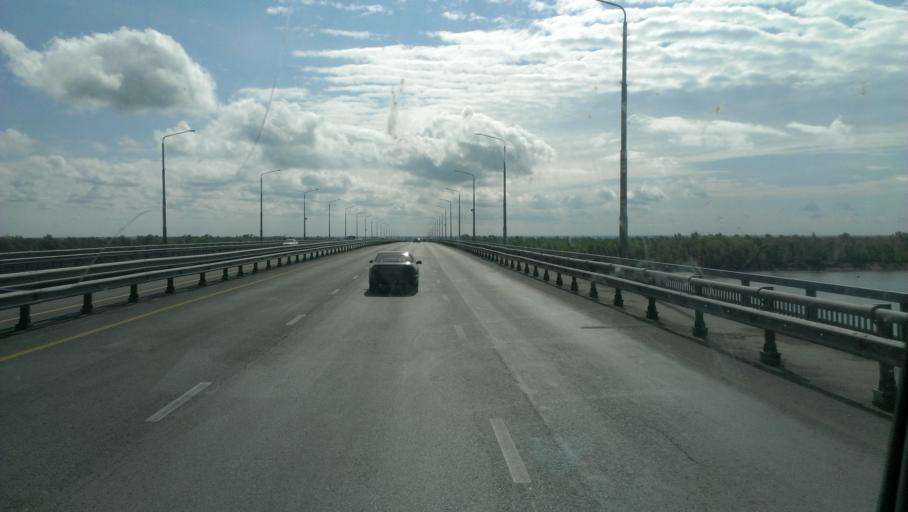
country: RU
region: Altai Krai
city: Zaton
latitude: 53.3244
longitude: 83.8003
